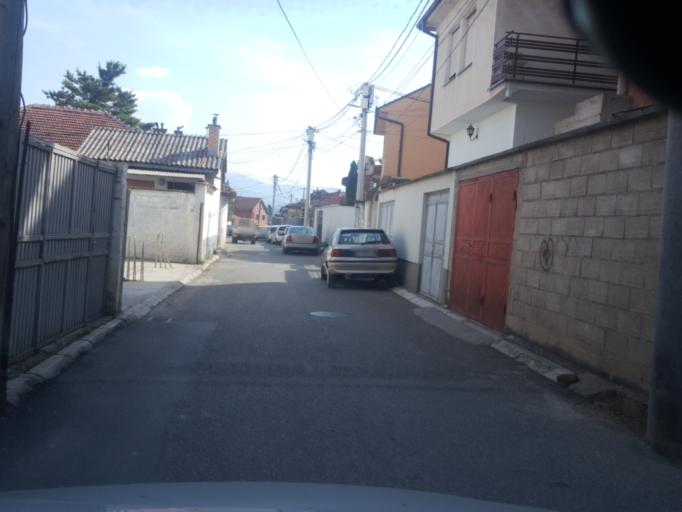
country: XK
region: Gjakova
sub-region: Komuna e Gjakoves
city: Gjakove
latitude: 42.3804
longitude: 20.4244
